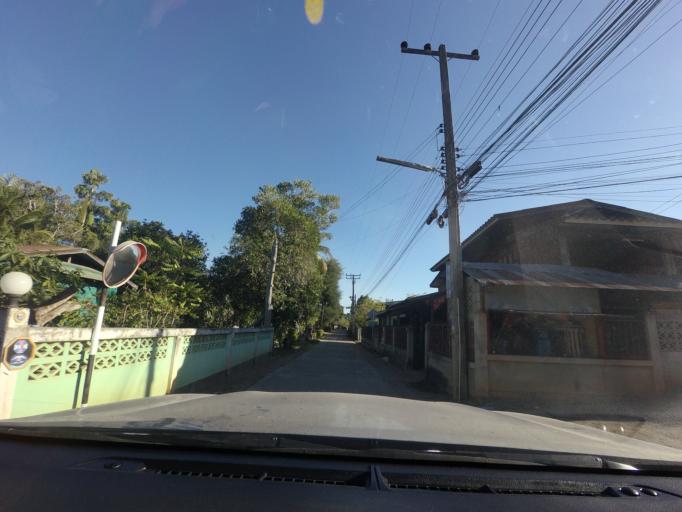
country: TH
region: Mae Hong Son
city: Wiang Nuea
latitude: 19.3938
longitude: 98.4217
